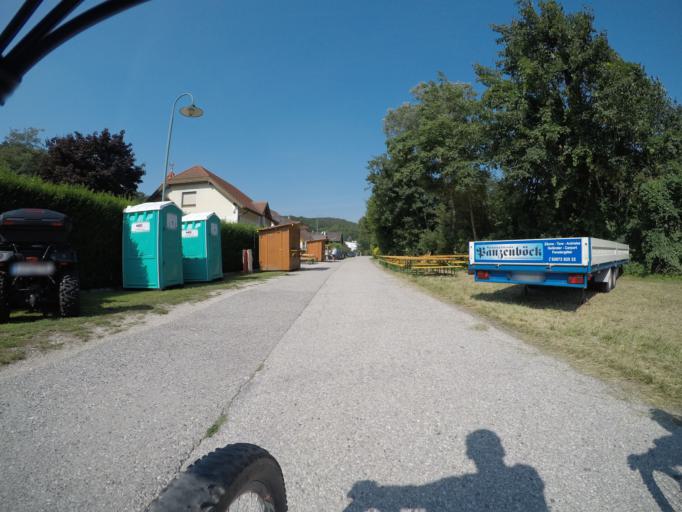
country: AT
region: Lower Austria
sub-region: Politischer Bezirk Baden
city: Hirtenberg
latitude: 47.9352
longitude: 16.1453
